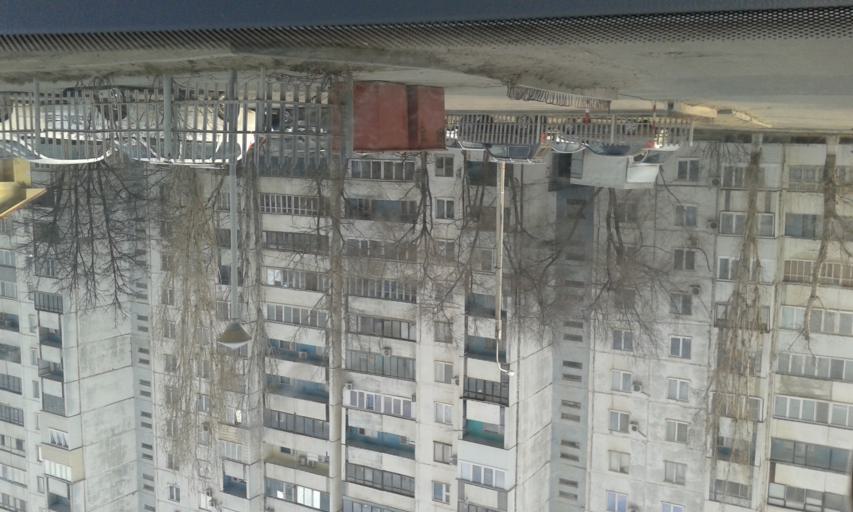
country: RU
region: Volgograd
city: Volgograd
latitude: 48.6547
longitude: 44.4347
